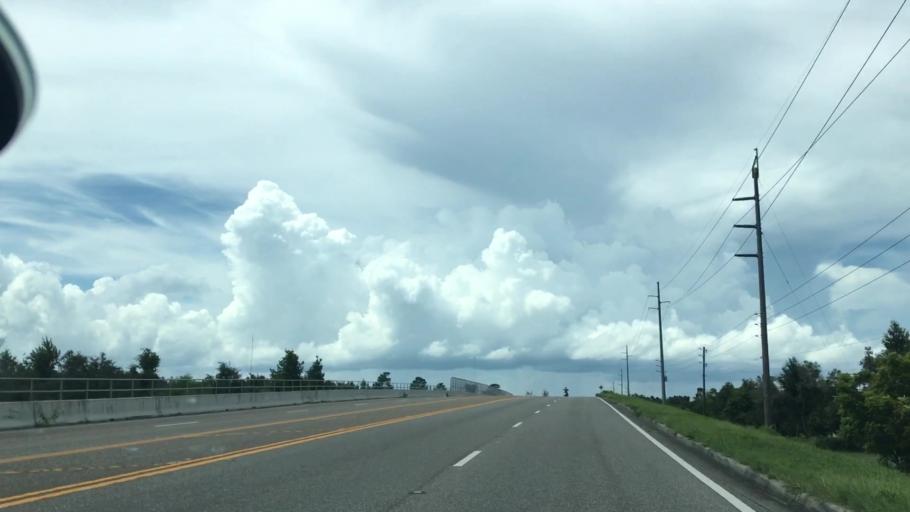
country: US
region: Florida
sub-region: Volusia County
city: Deltona
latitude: 28.8853
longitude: -81.2784
